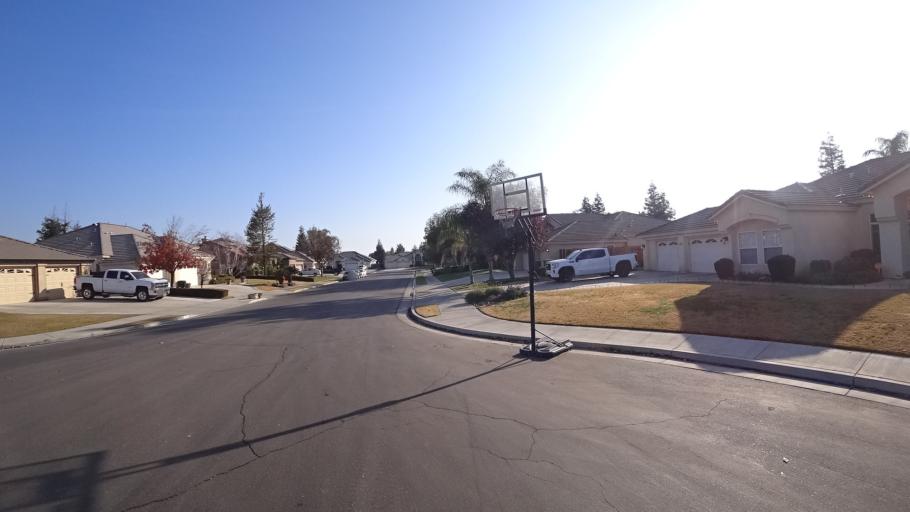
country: US
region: California
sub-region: Kern County
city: Greenacres
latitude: 35.3666
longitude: -119.1252
